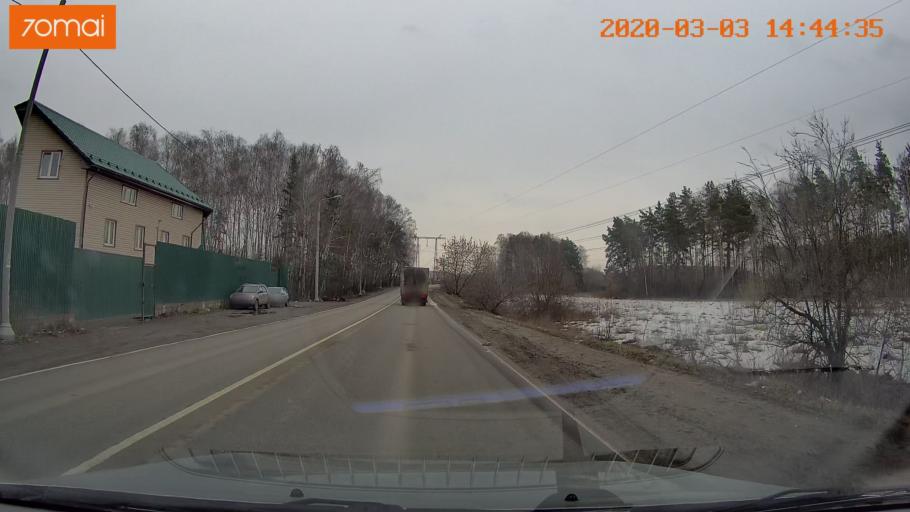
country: RU
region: Moskovskaya
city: Korenevo
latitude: 55.7017
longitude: 38.0333
